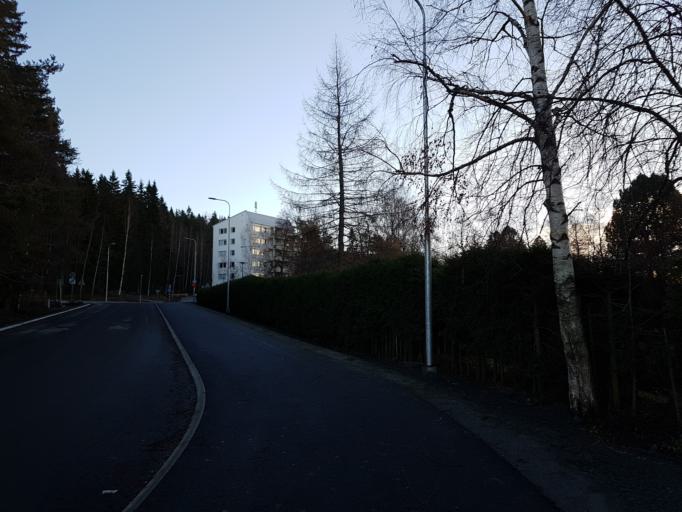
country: FI
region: Northern Savo
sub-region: Kuopio
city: Kuopio
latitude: 62.9337
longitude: 27.6318
